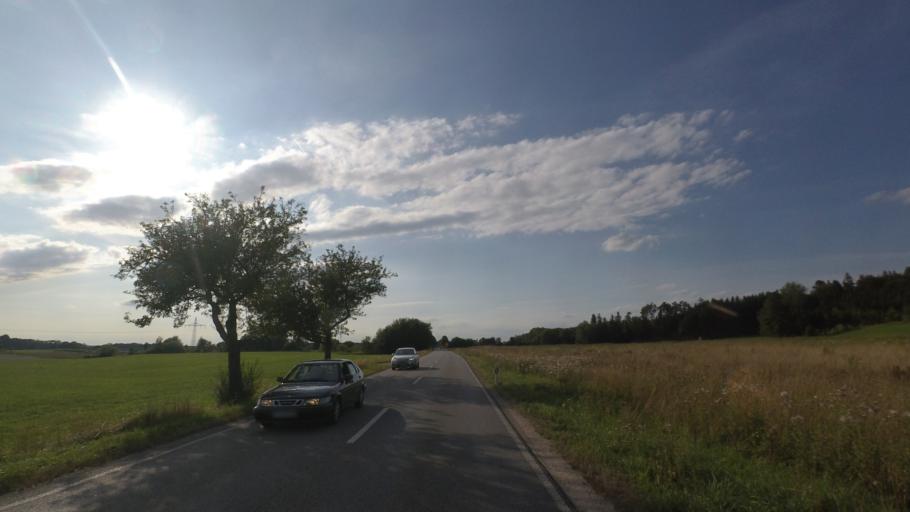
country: DE
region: Bavaria
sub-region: Upper Bavaria
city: Chieming
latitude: 47.9028
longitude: 12.5462
